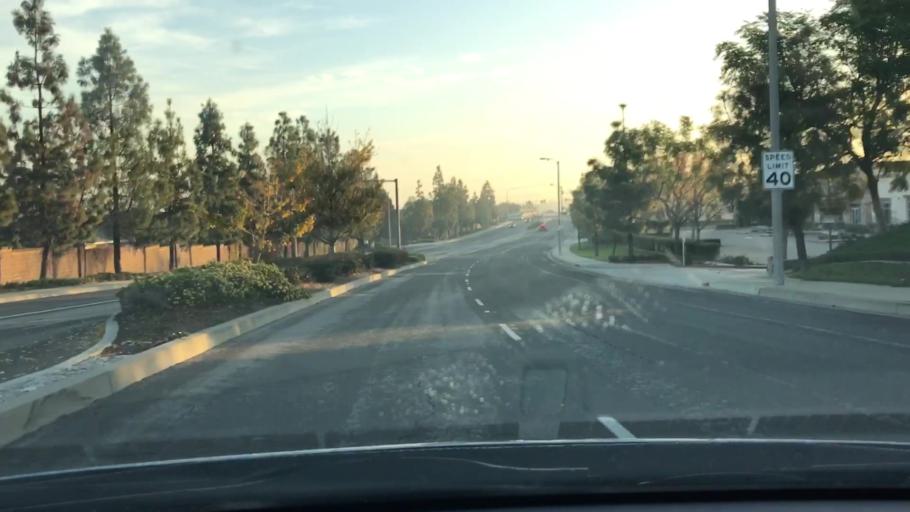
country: US
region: California
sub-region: San Bernardino County
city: Los Serranos
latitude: 33.9472
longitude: -117.6790
